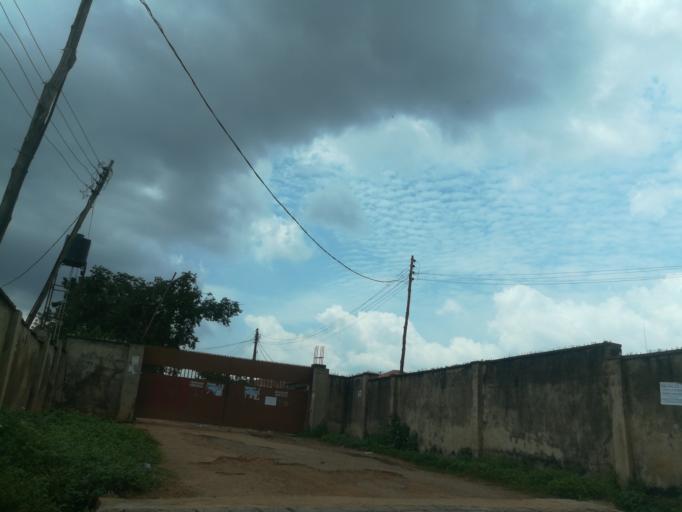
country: NG
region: Oyo
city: Ibadan
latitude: 7.4050
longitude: 3.9349
